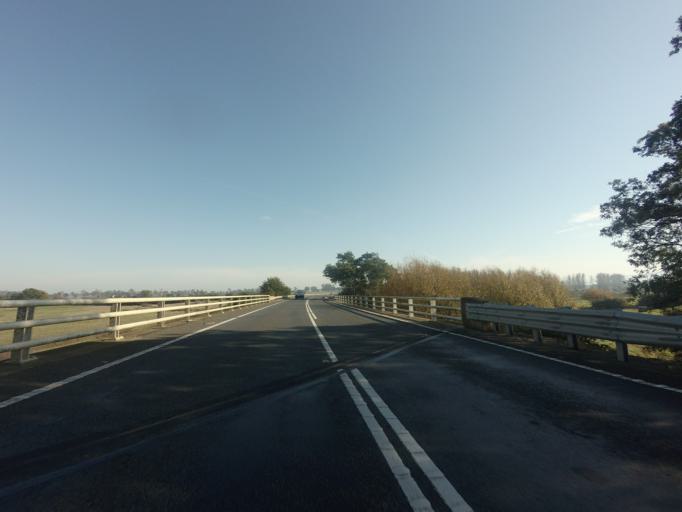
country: AU
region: Tasmania
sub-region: Northern Midlands
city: Longford
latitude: -41.5808
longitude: 147.1071
